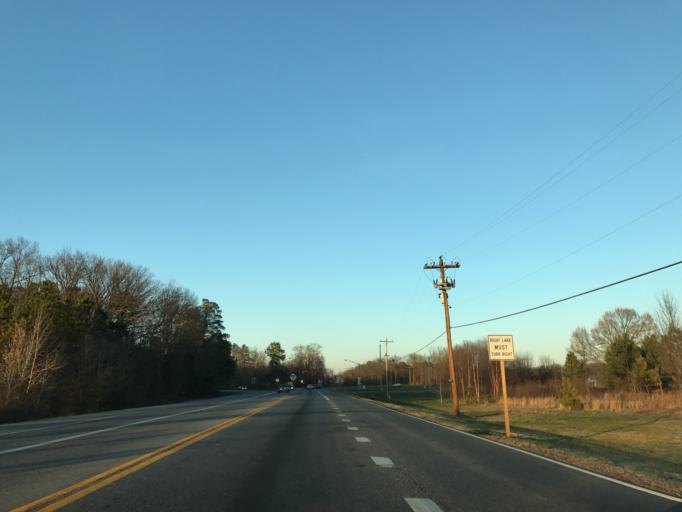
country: US
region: Maryland
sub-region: Talbot County
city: Easton
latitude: 38.7976
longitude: -76.0623
